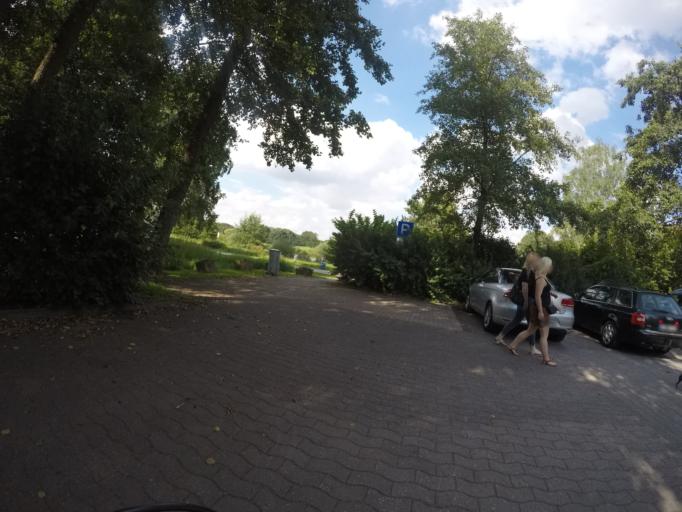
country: DE
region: North Rhine-Westphalia
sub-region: Regierungsbezirk Detmold
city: Bielefeld
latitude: 52.0546
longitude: 8.5680
